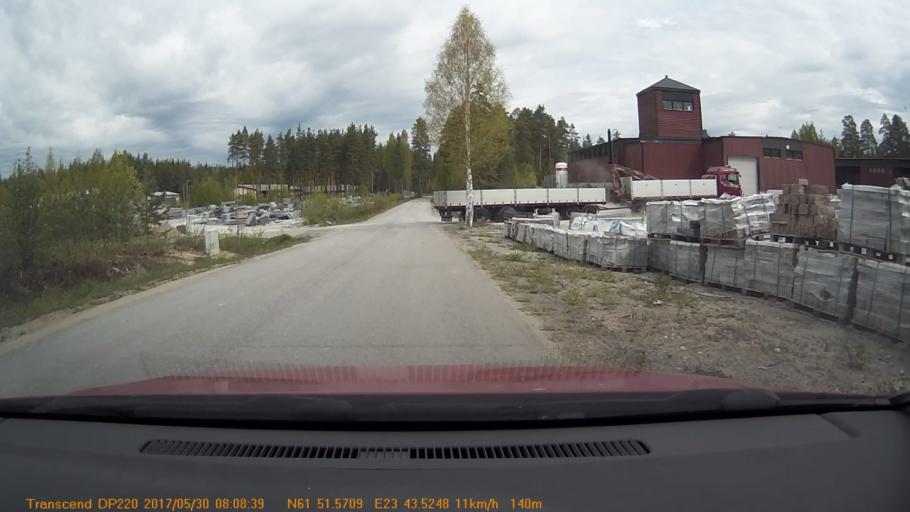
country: FI
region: Pirkanmaa
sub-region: Tampere
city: Kuru
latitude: 61.8595
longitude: 23.7253
